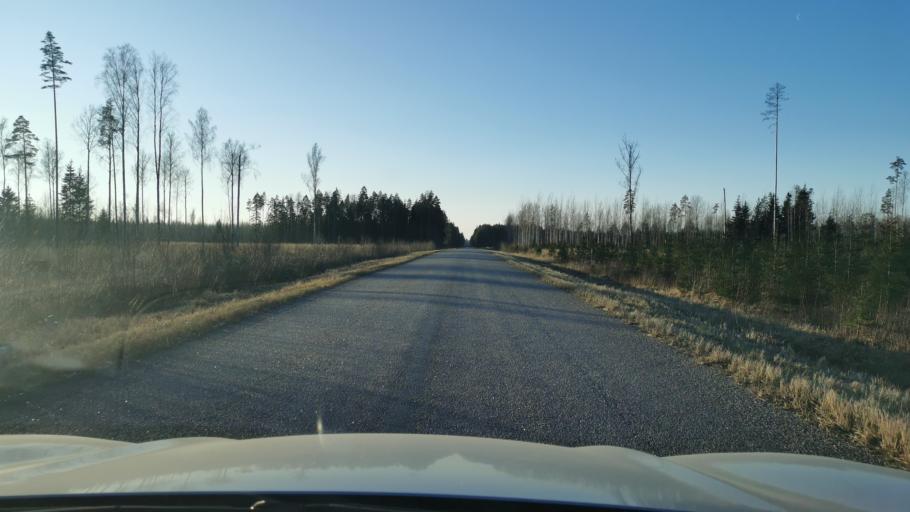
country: EE
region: Ida-Virumaa
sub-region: Kivioli linn
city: Kivioli
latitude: 59.2279
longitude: 26.9643
